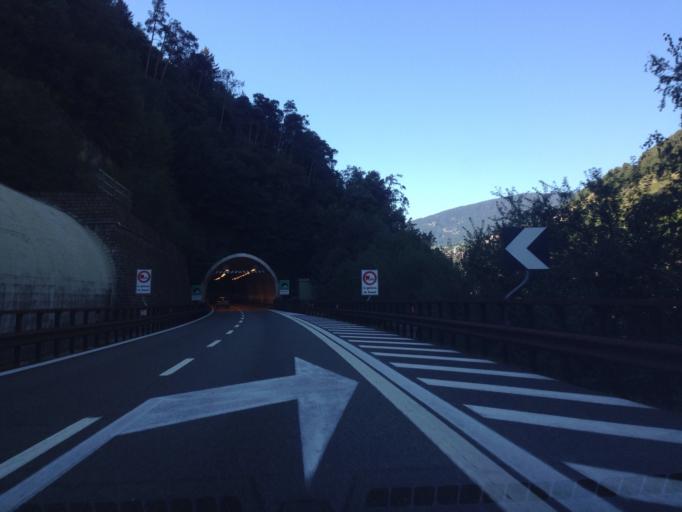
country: IT
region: Trentino-Alto Adige
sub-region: Bolzano
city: Velturno
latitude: 46.6523
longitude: 11.5918
